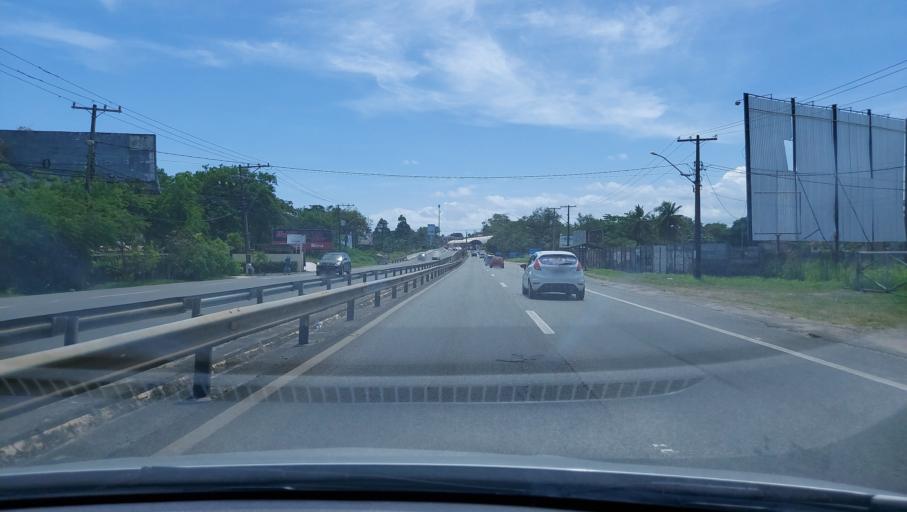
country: BR
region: Bahia
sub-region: Lauro De Freitas
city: Lauro de Freitas
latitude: -12.8605
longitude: -38.2882
